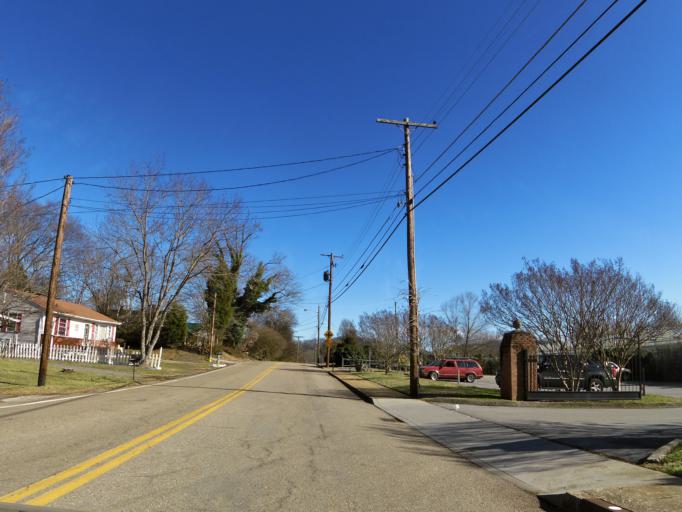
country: US
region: Tennessee
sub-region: Knox County
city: Knoxville
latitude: 35.9499
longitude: -83.9000
